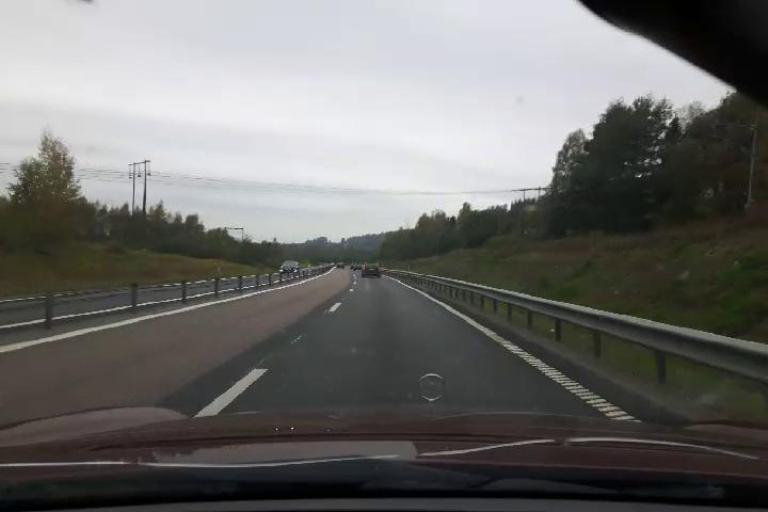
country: SE
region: Vaesternorrland
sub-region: OErnskoeldsviks Kommun
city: Ornskoldsvik
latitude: 63.2980
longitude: 18.6473
